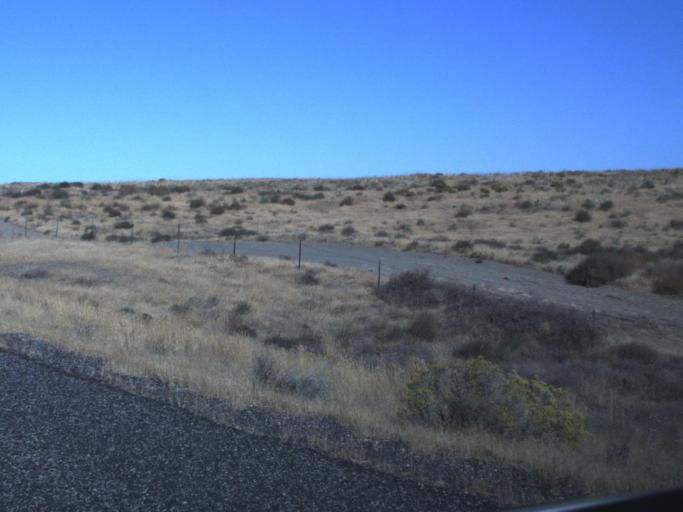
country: US
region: Washington
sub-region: Benton County
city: Benton City
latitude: 46.4982
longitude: -119.6077
